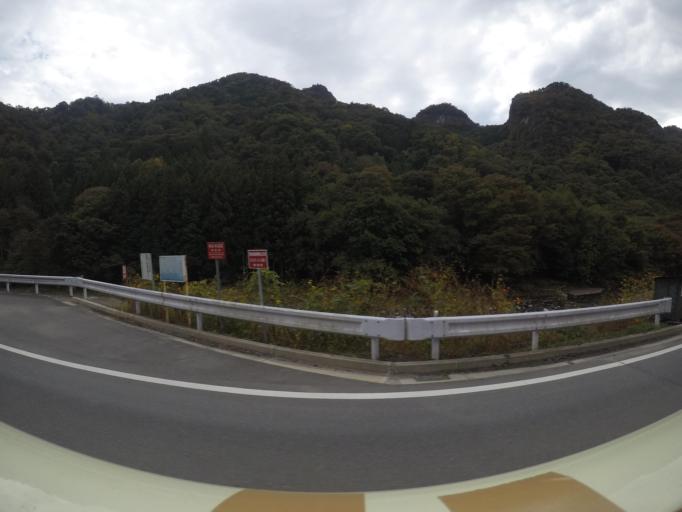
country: JP
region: Gunma
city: Tomioka
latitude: 36.0881
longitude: 138.8364
